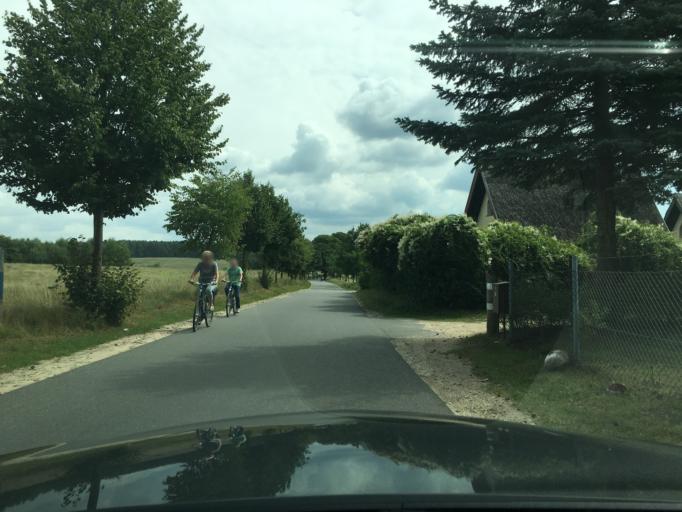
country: DE
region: Mecklenburg-Vorpommern
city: Waren
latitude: 53.5038
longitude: 12.7066
